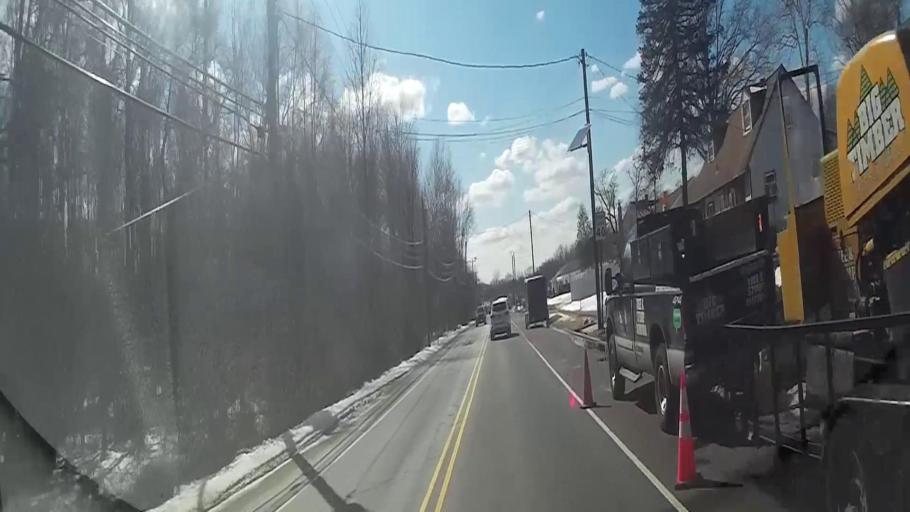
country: US
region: New Jersey
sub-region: Burlington County
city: Marlton
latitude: 39.8852
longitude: -74.8999
